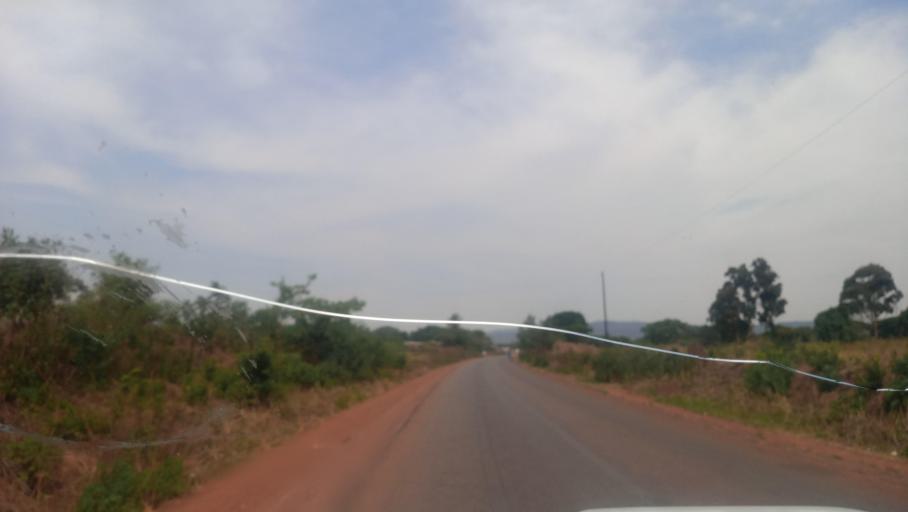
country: ZM
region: Northern
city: Mpika
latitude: -11.8329
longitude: 31.4195
